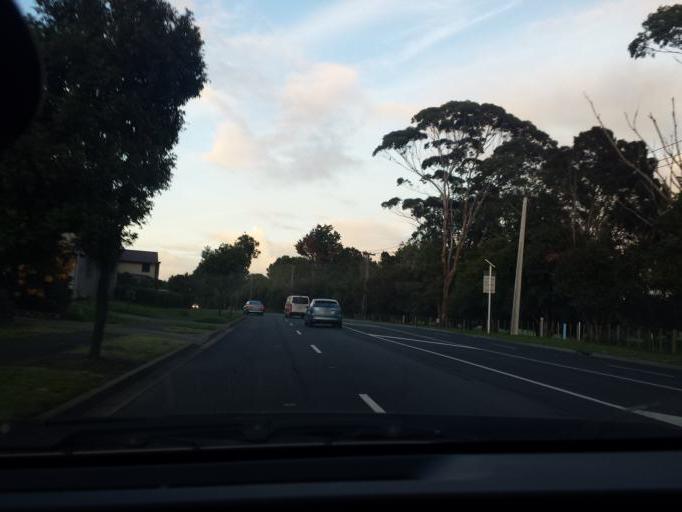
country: NZ
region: Auckland
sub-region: Auckland
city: Tamaki
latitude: -36.8843
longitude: 174.8362
